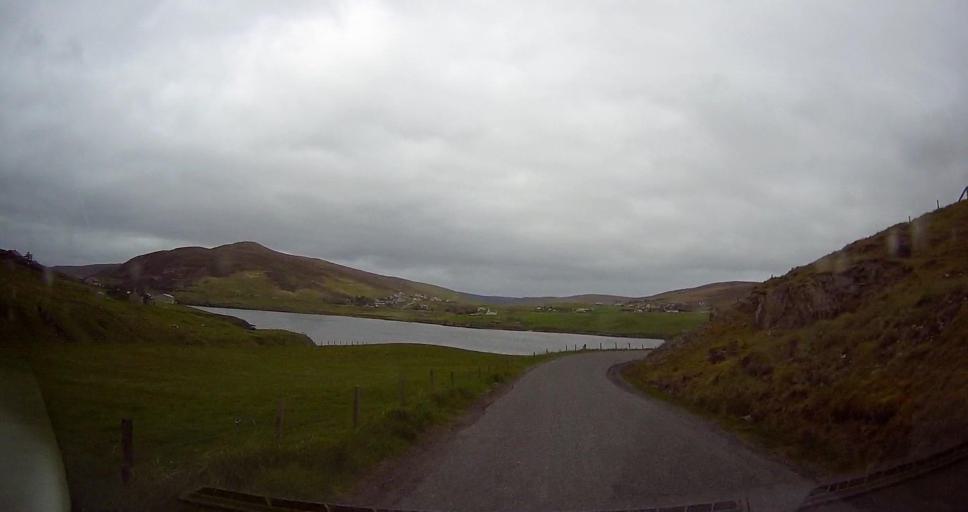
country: GB
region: Scotland
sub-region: Shetland Islands
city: Lerwick
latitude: 60.3469
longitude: -1.2711
